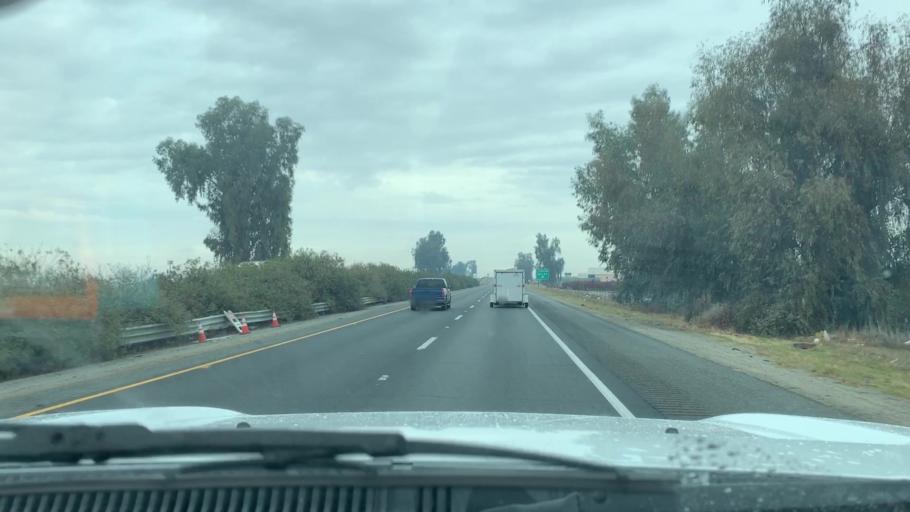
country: US
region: California
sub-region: Tulare County
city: Earlimart
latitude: 35.8282
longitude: -119.2590
